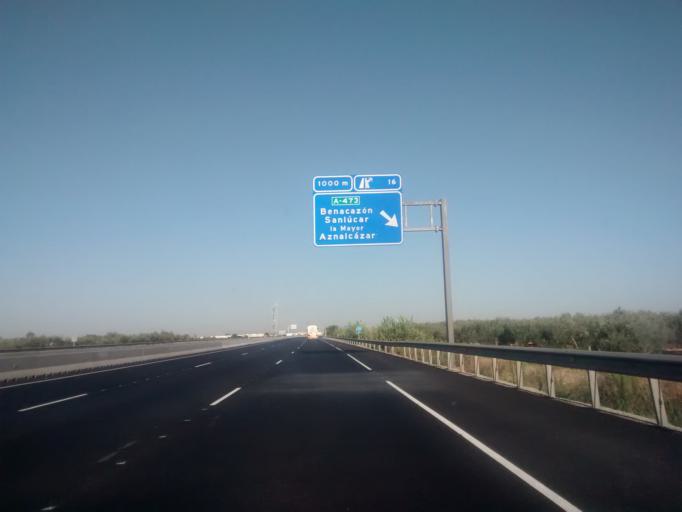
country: ES
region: Andalusia
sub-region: Provincia de Sevilla
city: Benacazon
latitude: 37.3580
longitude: -6.1837
